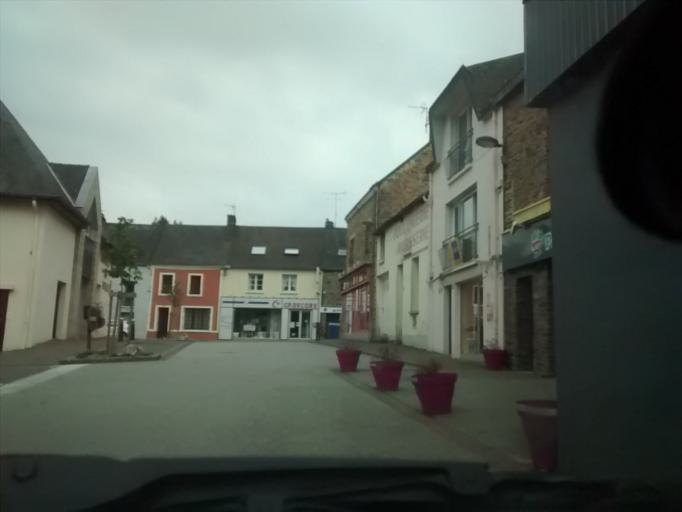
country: FR
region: Brittany
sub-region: Departement du Morbihan
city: Guer
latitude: 47.9034
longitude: -2.1205
